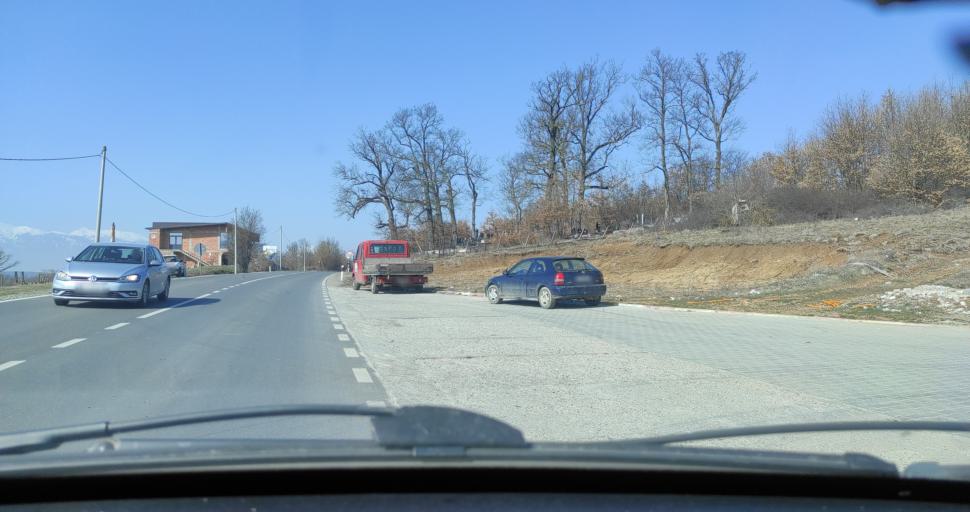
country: XK
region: Pec
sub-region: Komuna e Klines
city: Klina
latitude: 42.5907
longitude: 20.5548
